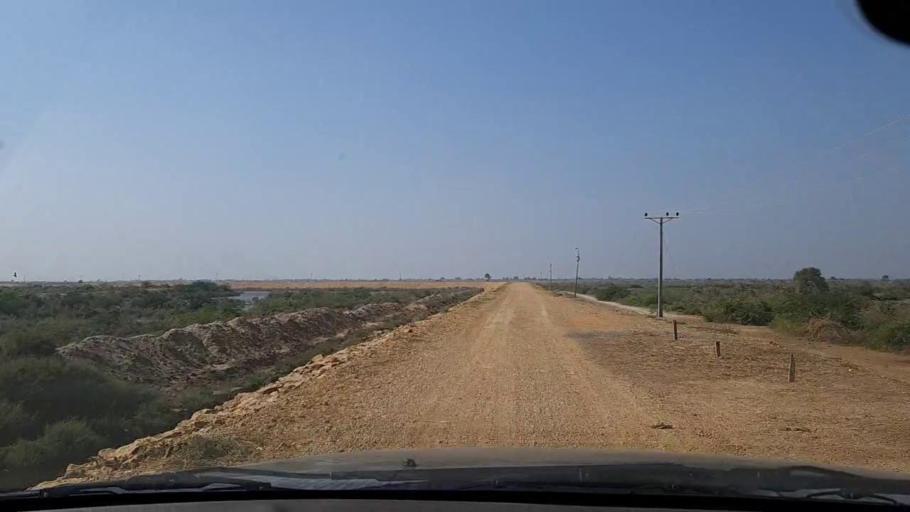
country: PK
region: Sindh
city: Chuhar Jamali
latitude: 24.4624
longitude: 67.8839
